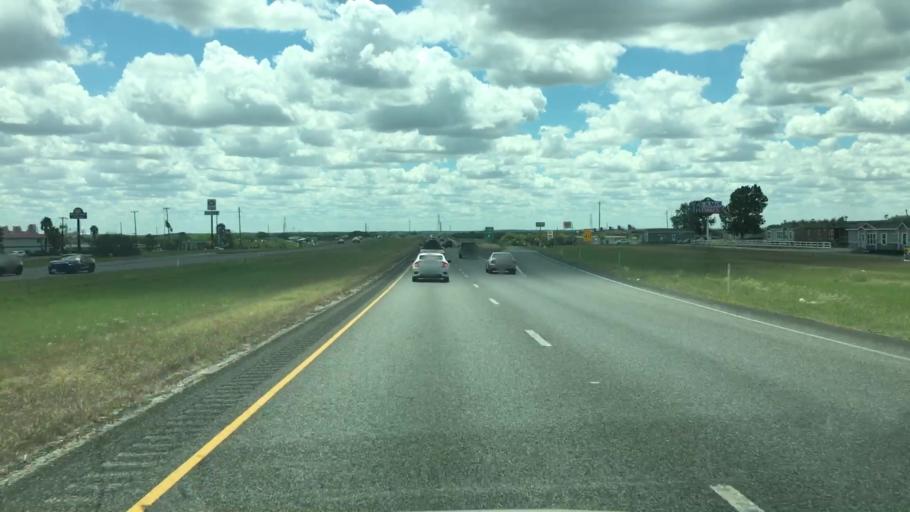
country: US
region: Texas
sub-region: Bexar County
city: Elmendorf
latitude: 29.2860
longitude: -98.3956
